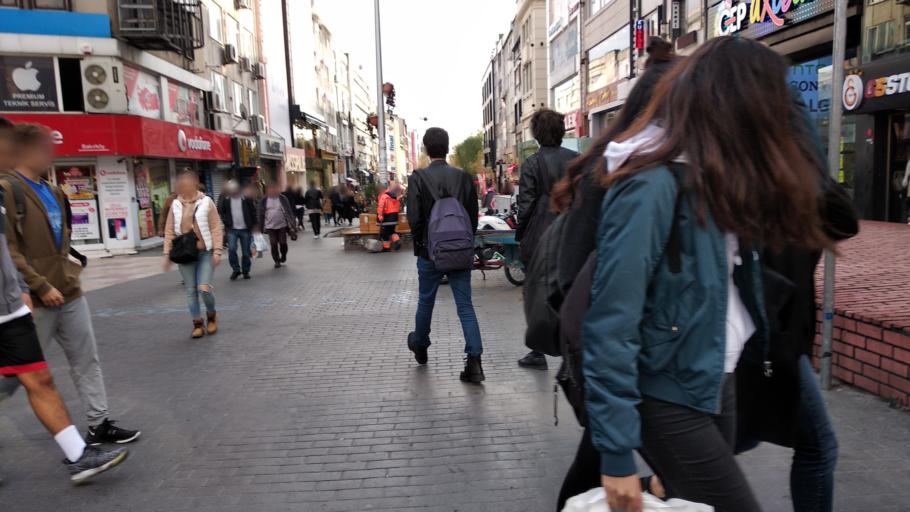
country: TR
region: Istanbul
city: Bahcelievler
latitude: 40.9785
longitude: 28.8744
